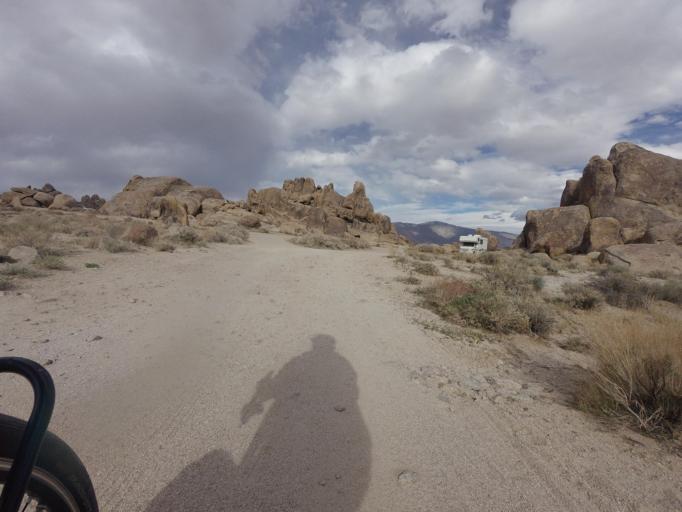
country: US
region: California
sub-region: Inyo County
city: Lone Pine
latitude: 36.5992
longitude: -118.1163
